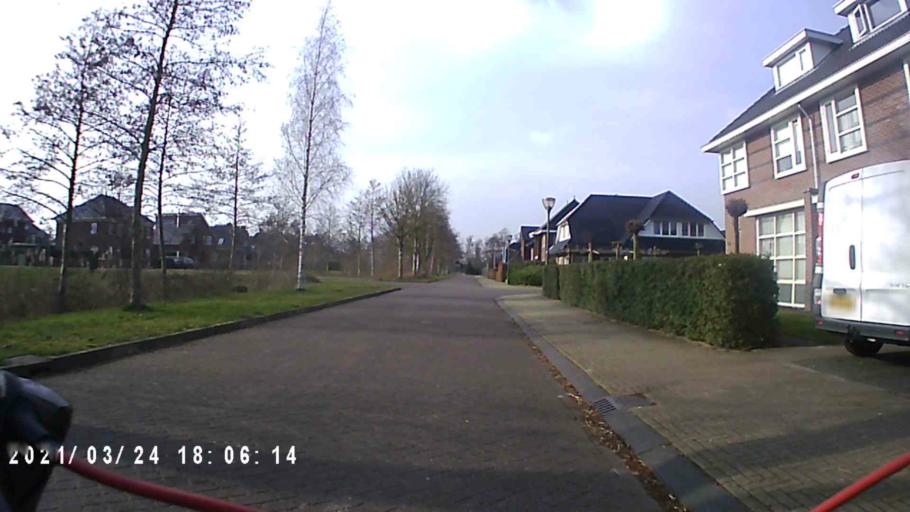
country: NL
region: Groningen
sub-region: Gemeente Leek
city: Leek
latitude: 53.1455
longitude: 6.3663
